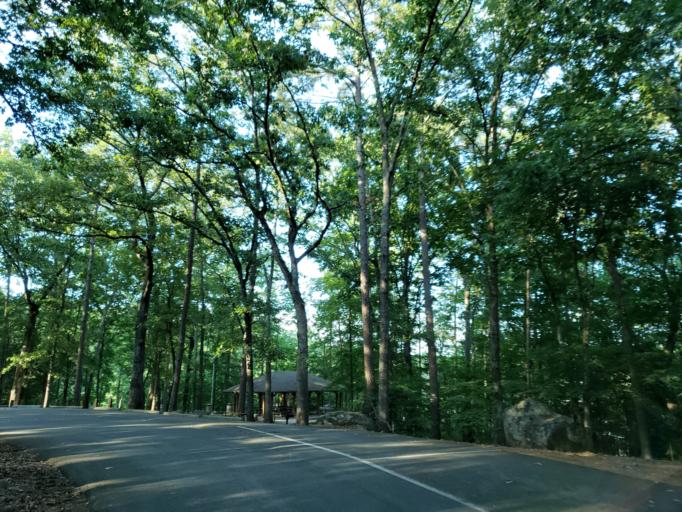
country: US
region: Georgia
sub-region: Bartow County
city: Emerson
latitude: 34.1723
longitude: -84.7341
